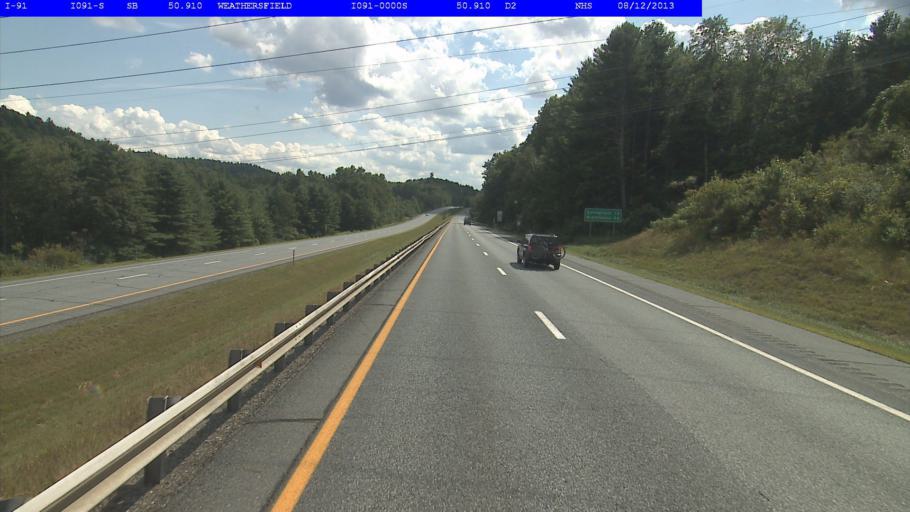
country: US
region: New Hampshire
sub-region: Sullivan County
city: Claremont
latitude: 43.3959
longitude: -72.4150
